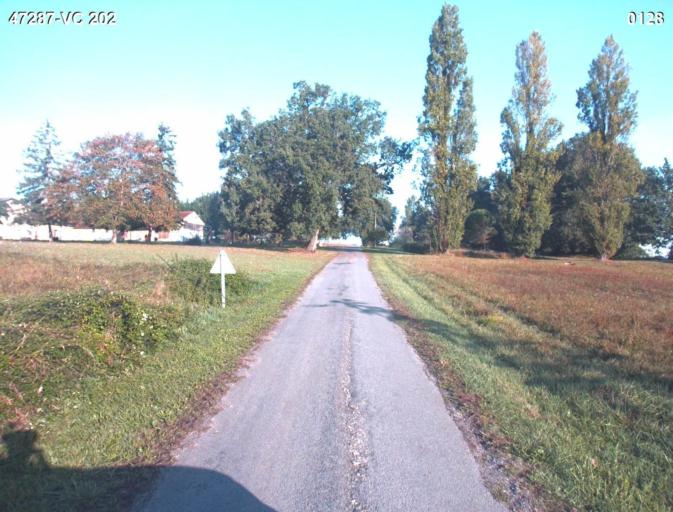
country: FR
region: Aquitaine
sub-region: Departement du Lot-et-Garonne
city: Laplume
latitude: 44.1121
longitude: 0.4678
